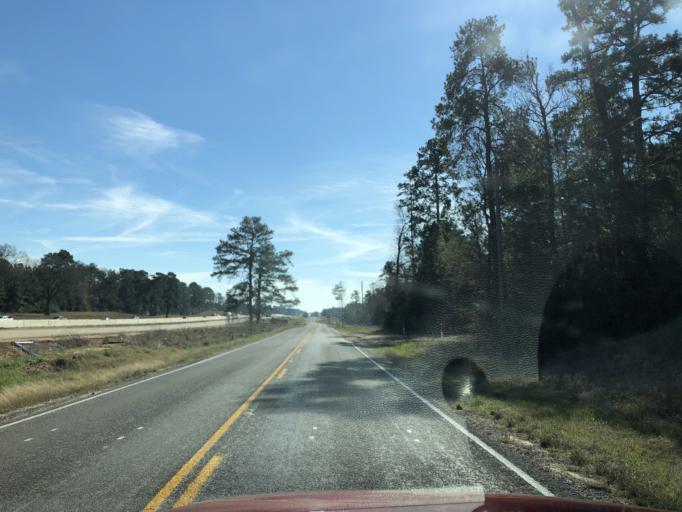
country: US
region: Texas
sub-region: Walker County
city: New Waverly
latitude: 30.6105
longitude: -95.5068
